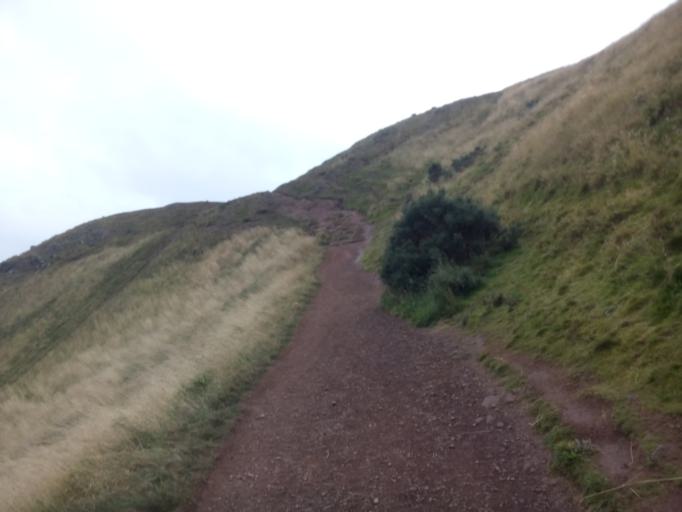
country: GB
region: Scotland
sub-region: West Lothian
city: Seafield
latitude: 55.9451
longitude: -3.1606
